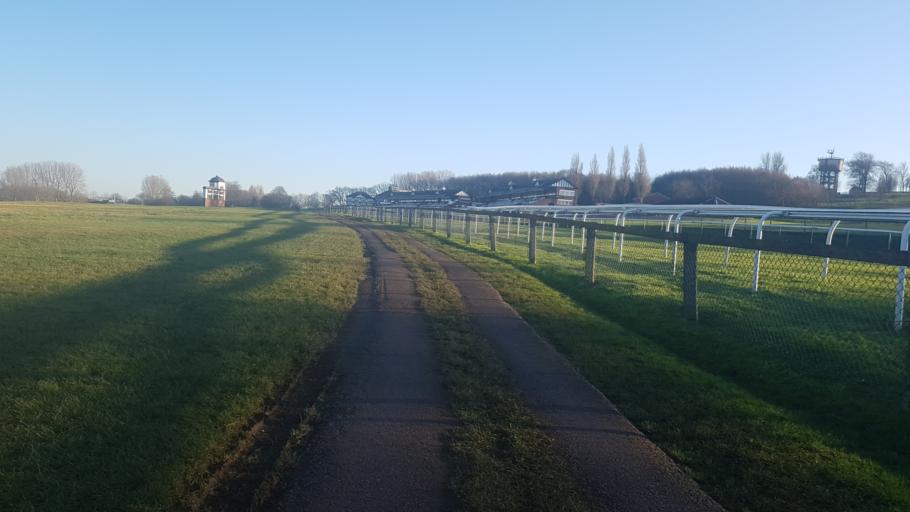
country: GB
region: England
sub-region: City and Borough of Wakefield
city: Pontefract
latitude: 53.6975
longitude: -1.3357
